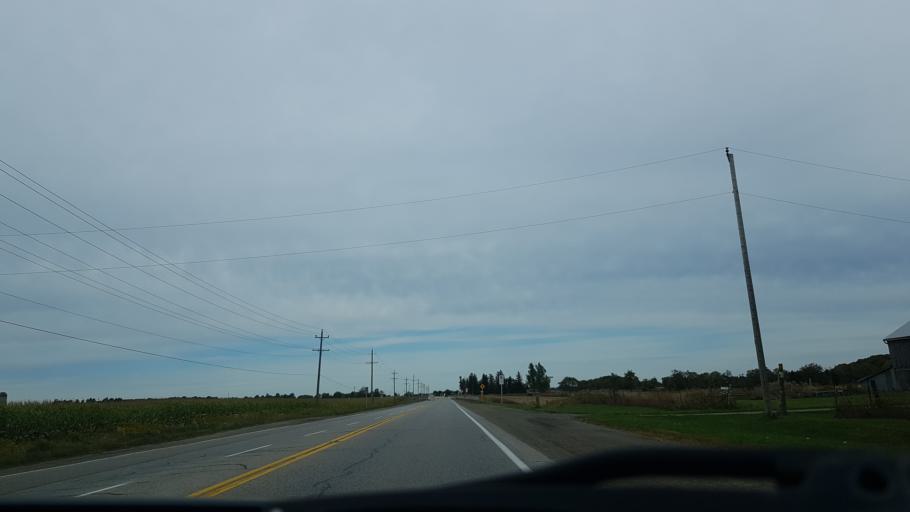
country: CA
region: Ontario
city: Orangeville
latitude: 43.8177
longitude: -80.0426
